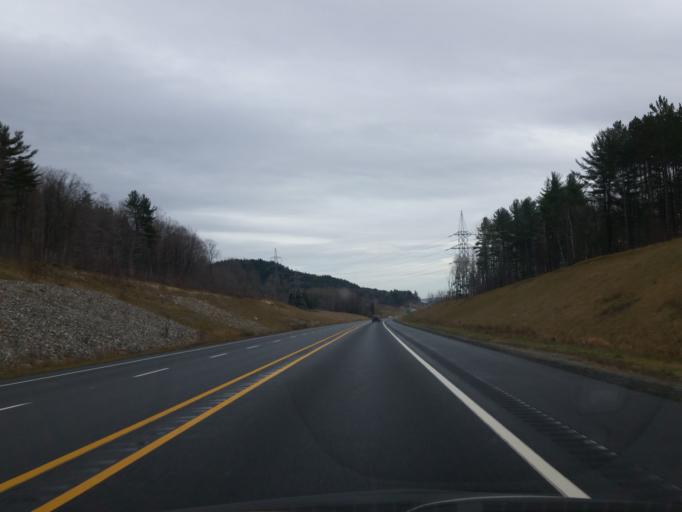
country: CA
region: Quebec
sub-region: Outaouais
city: Papineauville
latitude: 45.6647
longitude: -74.8890
